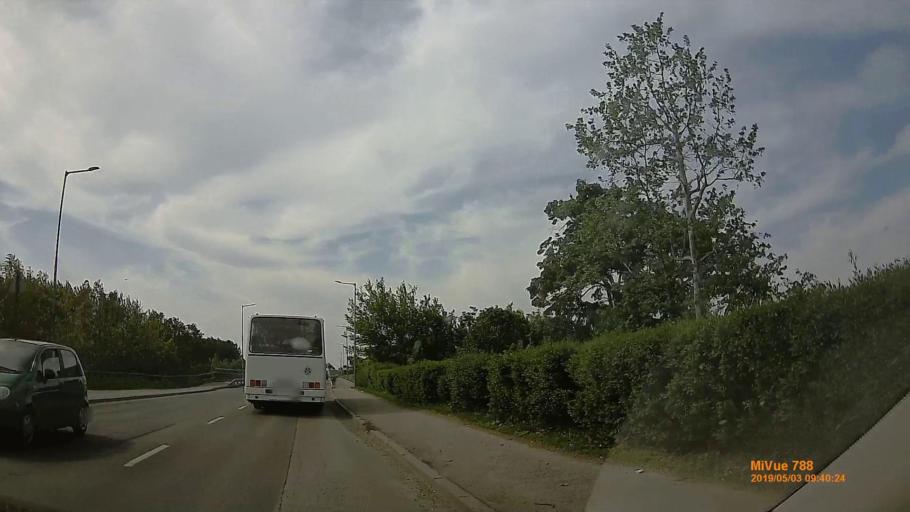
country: HU
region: Jasz-Nagykun-Szolnok
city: Szolnok
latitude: 47.1680
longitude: 20.2027
